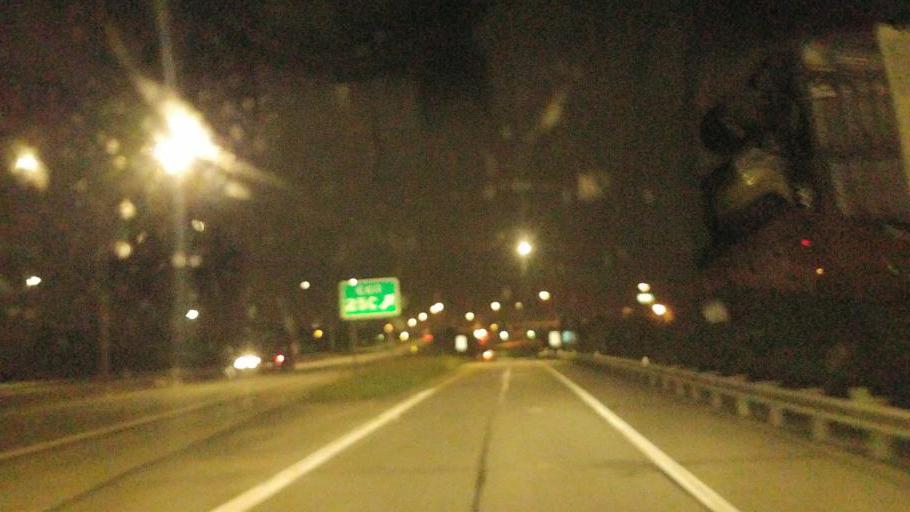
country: US
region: Ohio
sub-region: Cuyahoga County
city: Bedford Heights
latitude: 41.4191
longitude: -81.5195
